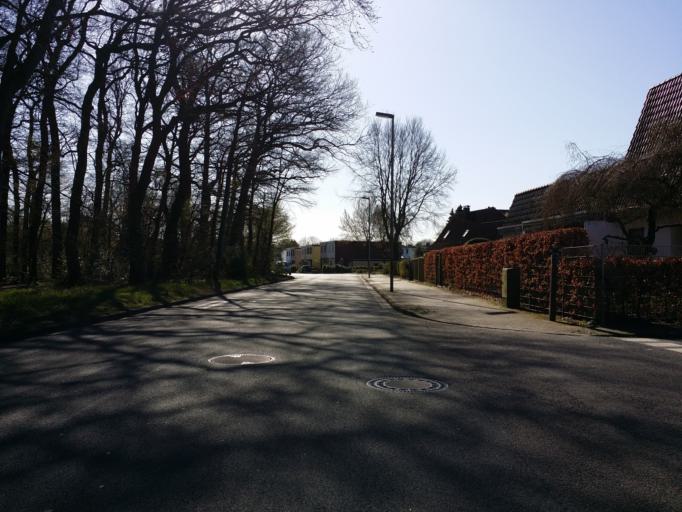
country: DE
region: Lower Saxony
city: Delmenhorst
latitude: 53.0233
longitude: 8.6604
